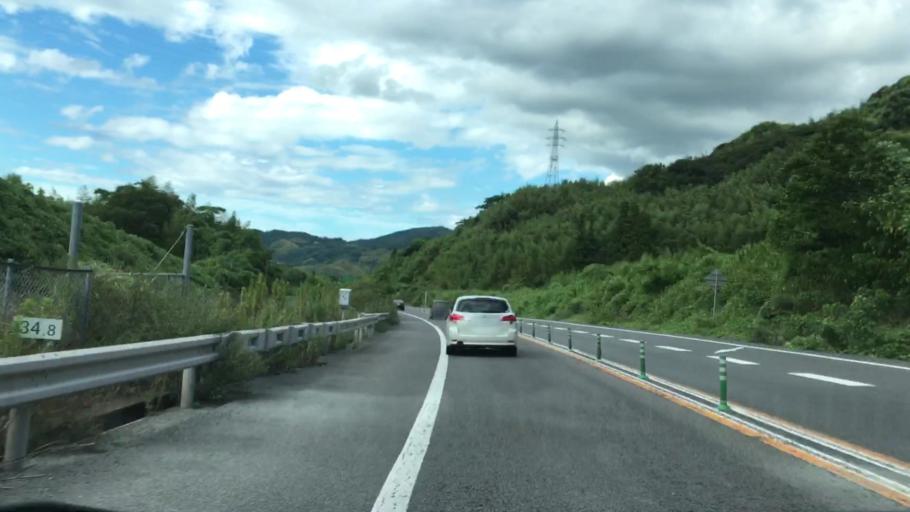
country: JP
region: Saga Prefecture
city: Karatsu
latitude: 33.4319
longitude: 130.0483
